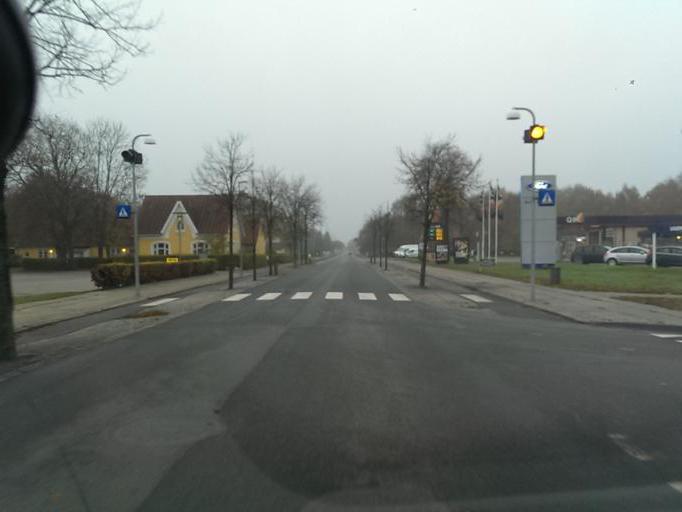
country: DK
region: South Denmark
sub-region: Esbjerg Kommune
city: Bramming
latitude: 55.4669
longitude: 8.6888
